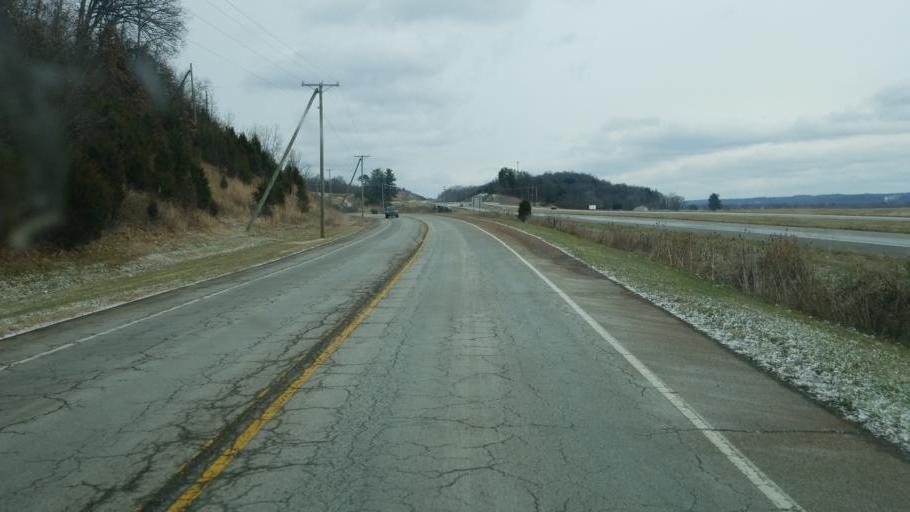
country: US
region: Ohio
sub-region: Muskingum County
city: Frazeysburg
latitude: 40.1137
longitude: -82.1605
